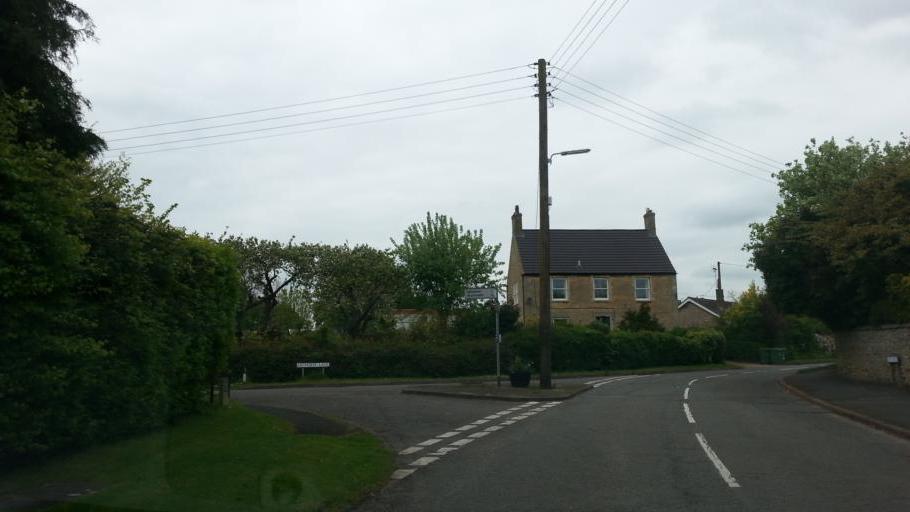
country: GB
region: England
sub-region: Lincolnshire
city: Bourne
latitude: 52.7381
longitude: -0.3775
